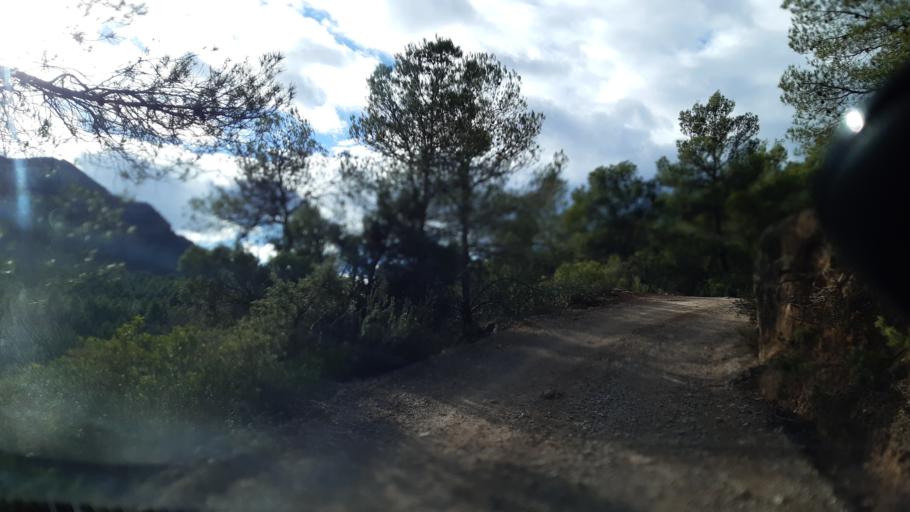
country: ES
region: Aragon
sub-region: Provincia de Teruel
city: Valderrobres
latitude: 40.8595
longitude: 0.2377
